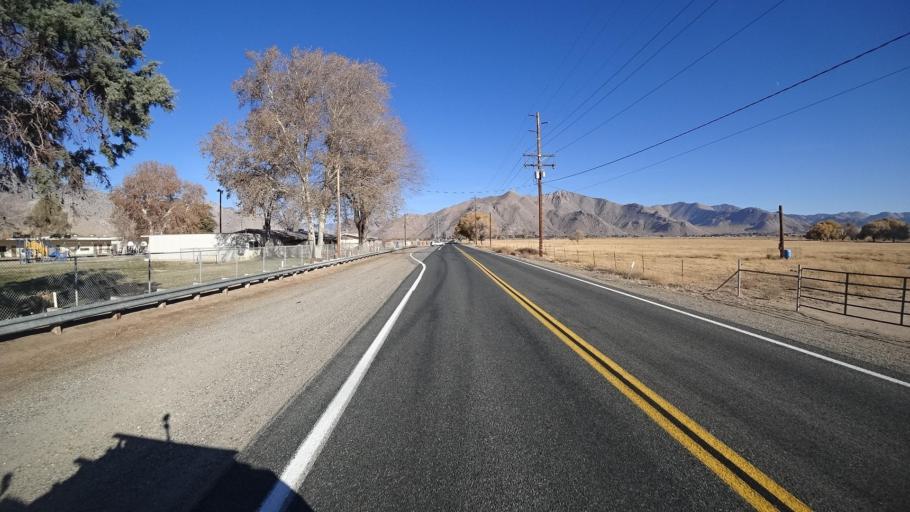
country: US
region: California
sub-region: Kern County
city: Weldon
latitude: 35.6656
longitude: -118.2914
